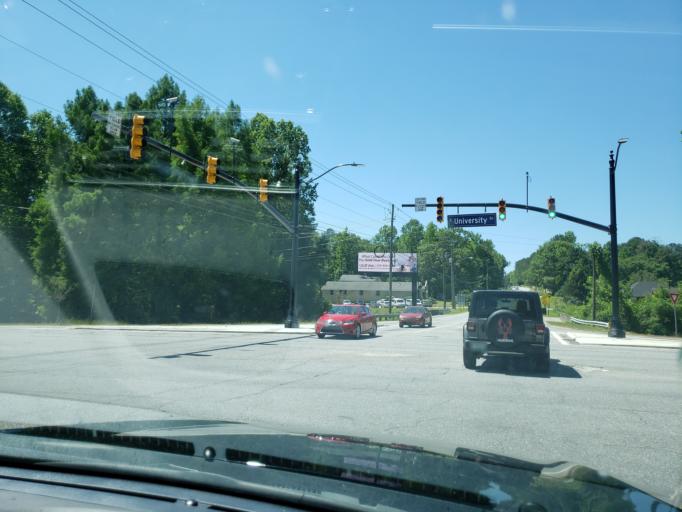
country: US
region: Alabama
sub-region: Lee County
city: Auburn
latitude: 32.6368
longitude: -85.4817
